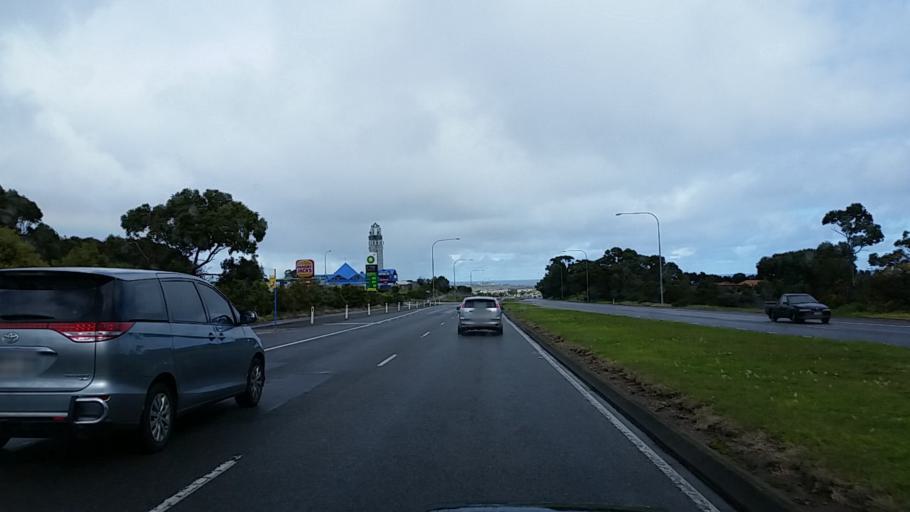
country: AU
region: South Australia
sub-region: Marion
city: Happy Valley
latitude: -35.0739
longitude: 138.5236
